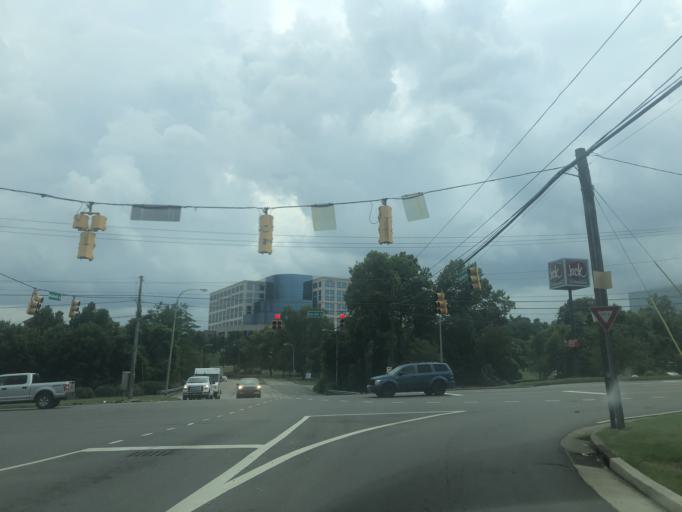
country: US
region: Tennessee
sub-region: Davidson County
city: Lakewood
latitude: 36.1531
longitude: -86.6832
